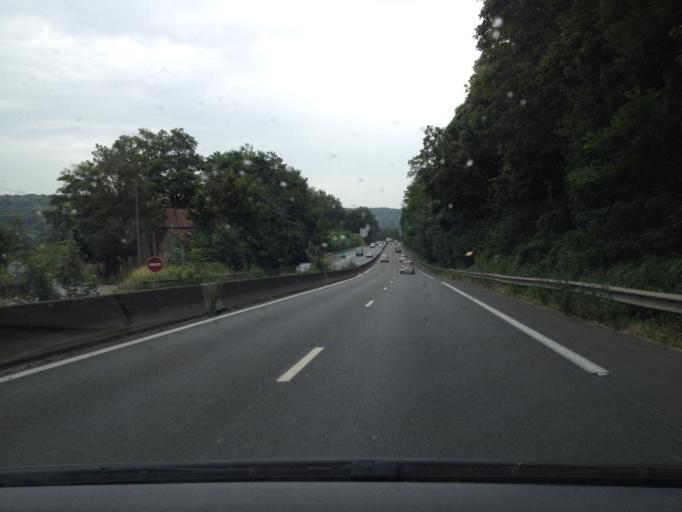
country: FR
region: Ile-de-France
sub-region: Departement de l'Essonne
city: Bievres
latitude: 48.7496
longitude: 2.2082
